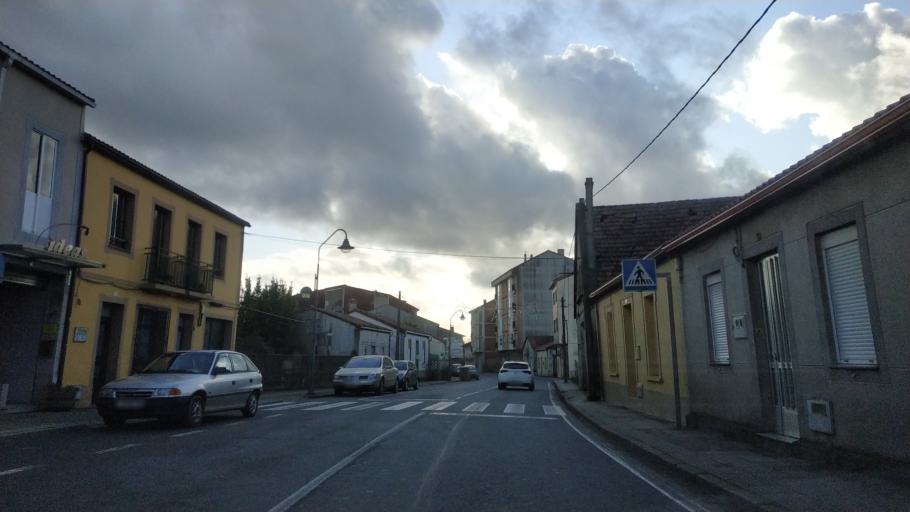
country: ES
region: Galicia
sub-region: Provincia da Coruna
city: Arzua
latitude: 42.9243
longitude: -8.1648
